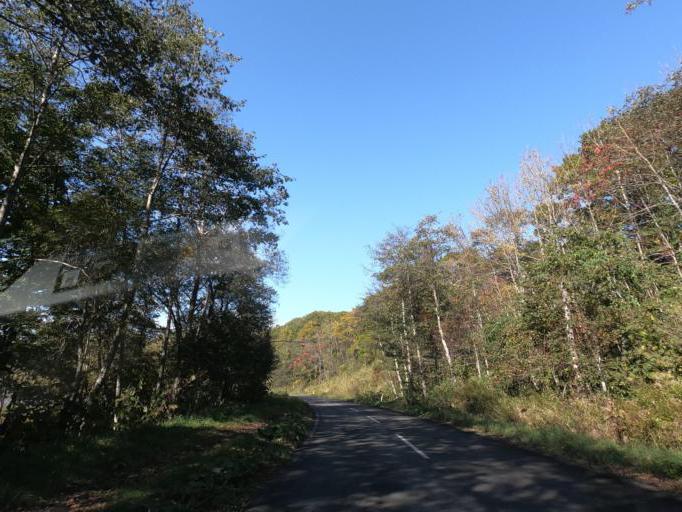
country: JP
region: Hokkaido
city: Obihiro
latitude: 42.6048
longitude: 143.5517
